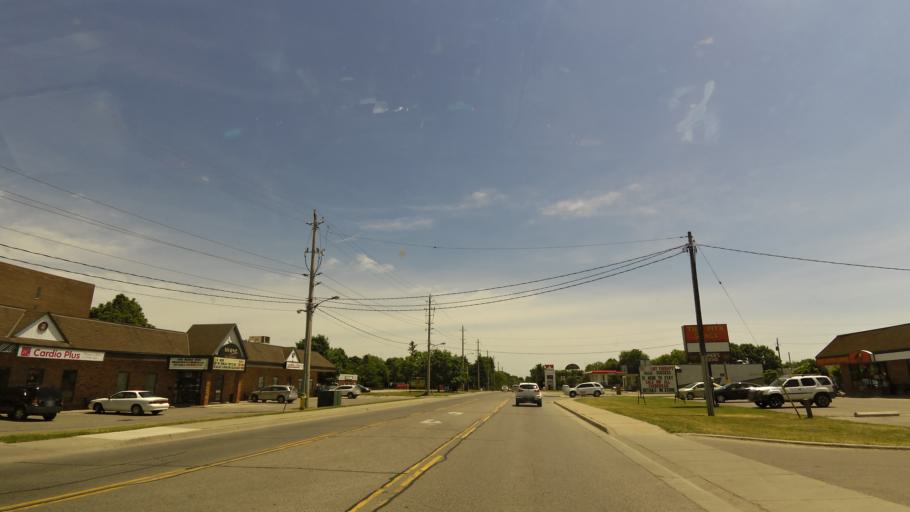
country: CA
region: Ontario
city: Ingersoll
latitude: 42.8757
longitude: -80.7437
